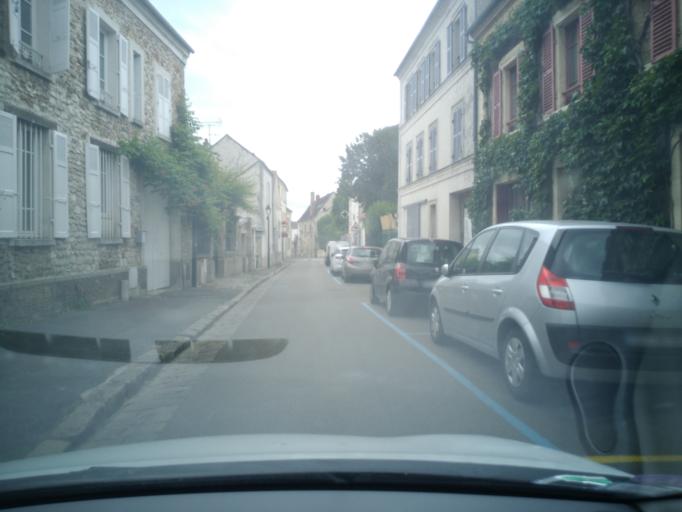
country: FR
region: Ile-de-France
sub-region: Departement des Yvelines
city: Crespieres
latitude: 48.8832
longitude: 1.9221
